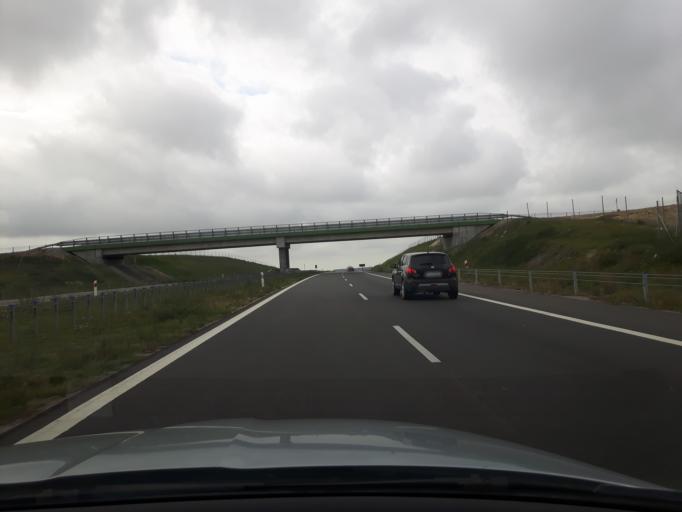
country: PL
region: Swietokrzyskie
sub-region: Powiat jedrzejowski
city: Sobkow
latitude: 50.7175
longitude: 20.4090
